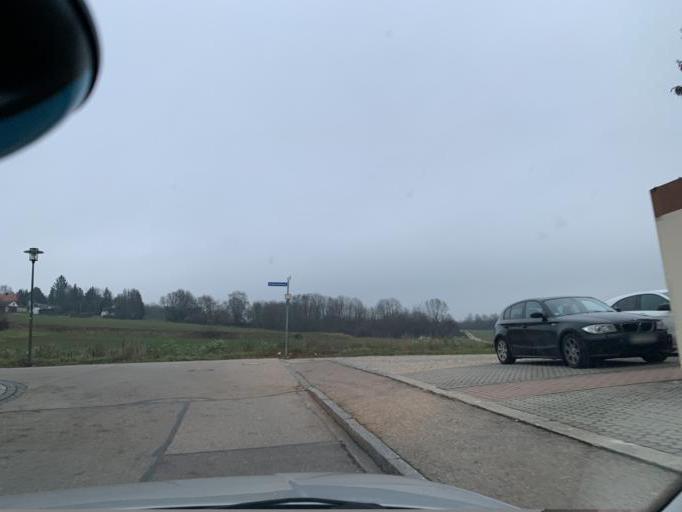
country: DE
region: Bavaria
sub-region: Upper Bavaria
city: Hepberg
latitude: 48.8206
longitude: 11.4667
